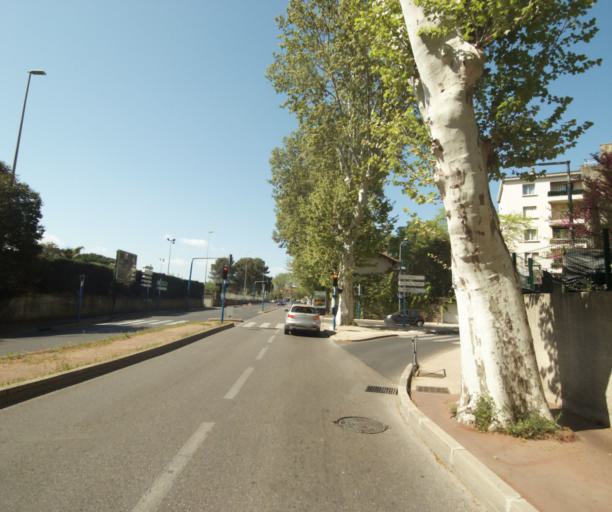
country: FR
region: Languedoc-Roussillon
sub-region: Departement de l'Herault
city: Montpellier
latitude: 43.6212
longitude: 3.8647
